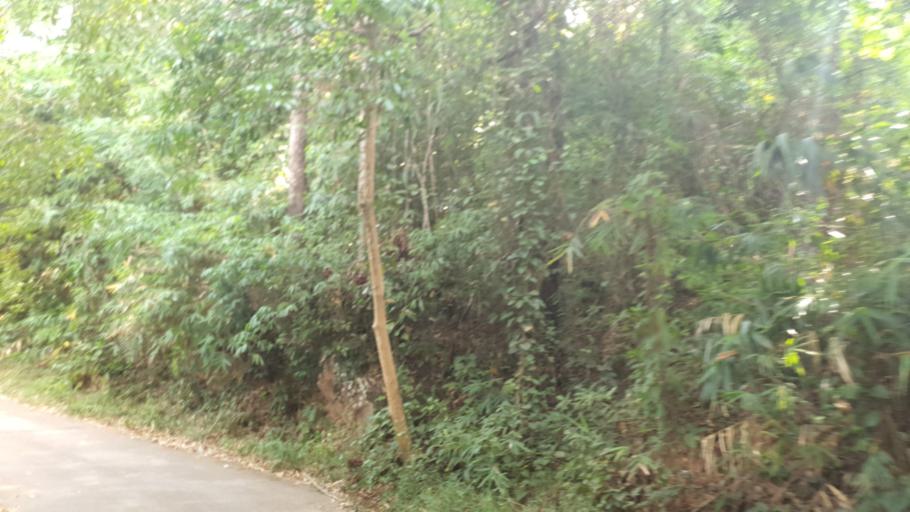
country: TH
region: Changwat Bueng Kan
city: Si Wilai
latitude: 18.2707
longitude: 103.7967
